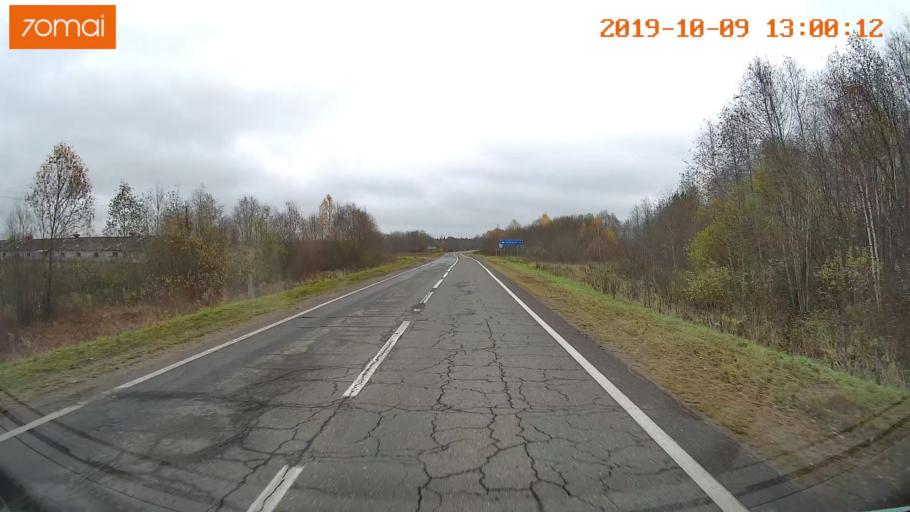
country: RU
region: Jaroslavl
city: Prechistoye
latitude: 58.3792
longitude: 40.4768
